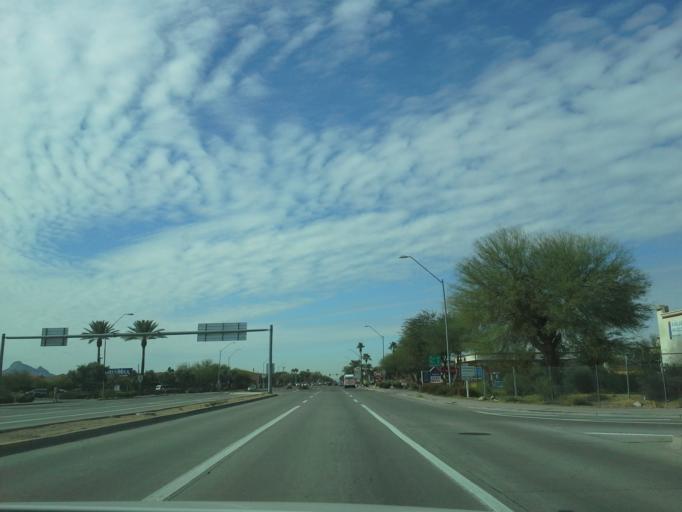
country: US
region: Arizona
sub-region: Maricopa County
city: Paradise Valley
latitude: 33.6407
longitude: -112.0033
